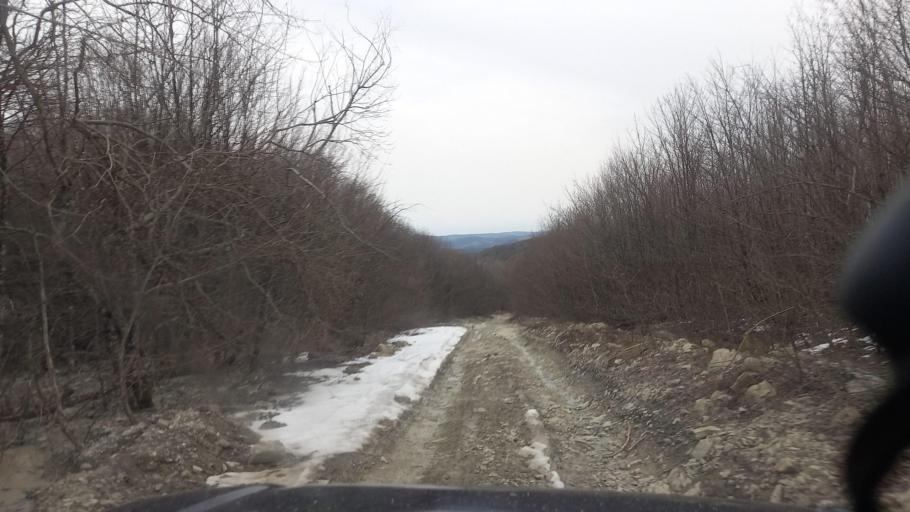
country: RU
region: Krasnodarskiy
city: Pshada
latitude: 44.5935
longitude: 38.3060
